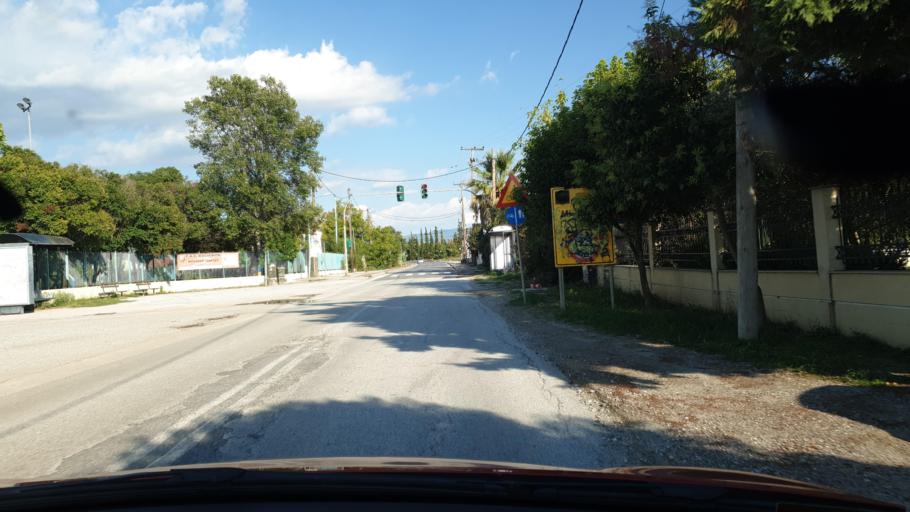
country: GR
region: Central Macedonia
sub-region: Nomos Thessalonikis
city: Vasilika
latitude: 40.4811
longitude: 23.1229
